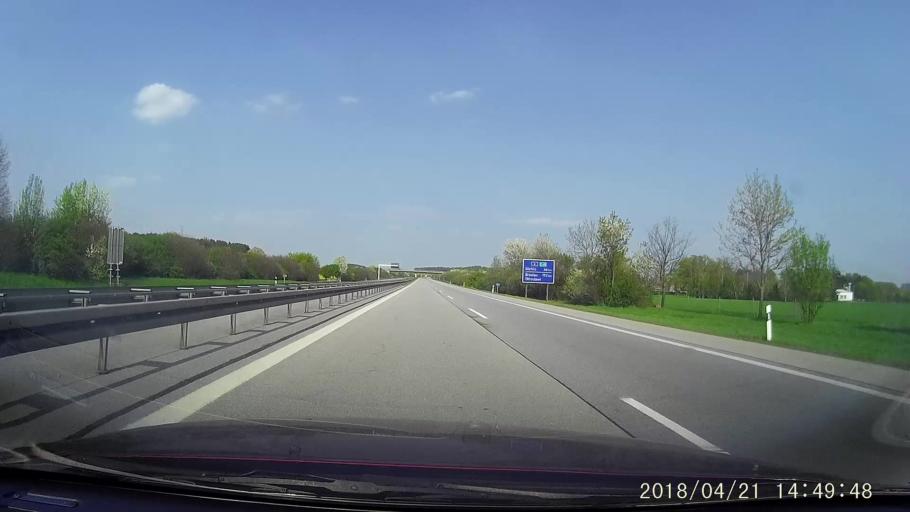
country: DE
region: Saxony
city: Kubschutz
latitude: 51.1993
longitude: 14.4771
